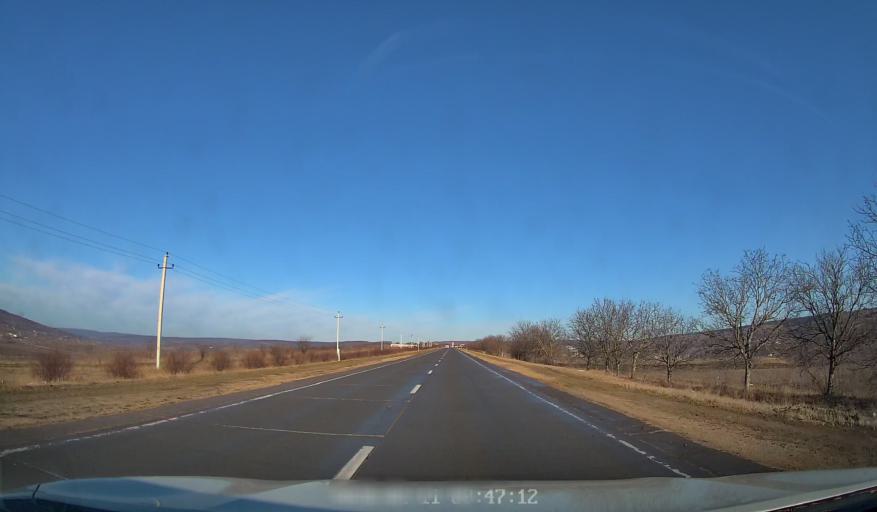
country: MD
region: Straseni
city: Straseni
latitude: 47.2677
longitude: 28.5891
